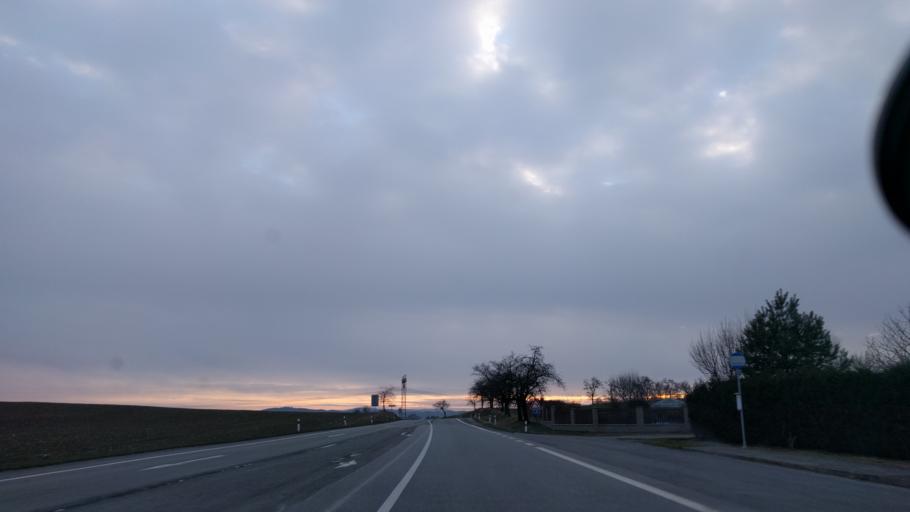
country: CZ
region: Jihocesky
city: Radomysl
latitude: 49.2830
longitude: 13.9538
